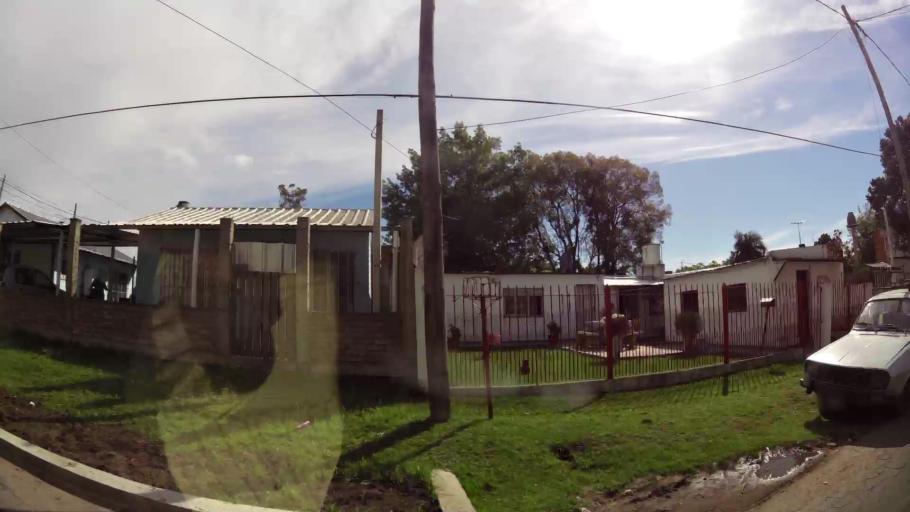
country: AR
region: Buenos Aires
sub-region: Partido de Almirante Brown
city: Adrogue
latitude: -34.8166
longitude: -58.3535
